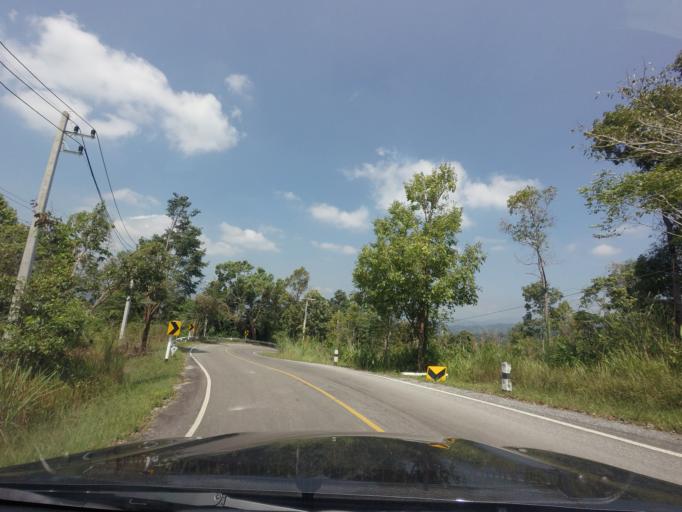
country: TH
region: Loei
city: Na Haeo
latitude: 17.4885
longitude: 100.9025
